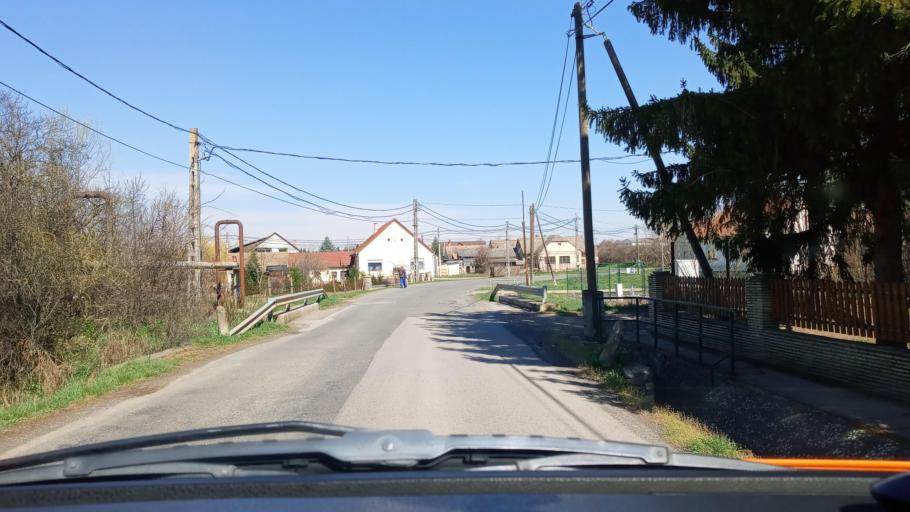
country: HU
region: Baranya
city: Boly
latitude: 46.0299
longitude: 18.4597
